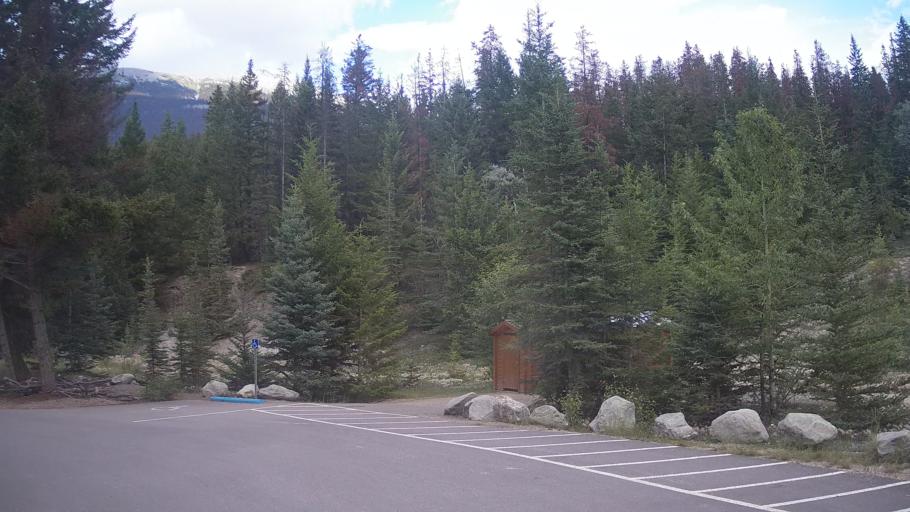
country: CA
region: Alberta
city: Jasper Park Lodge
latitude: 52.9211
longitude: -118.0166
